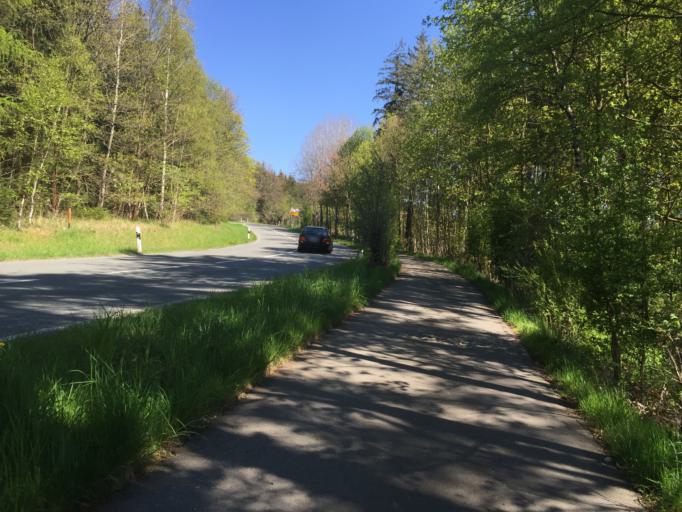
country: DE
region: Saxony
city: Neuensalz
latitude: 50.5046
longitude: 12.1937
